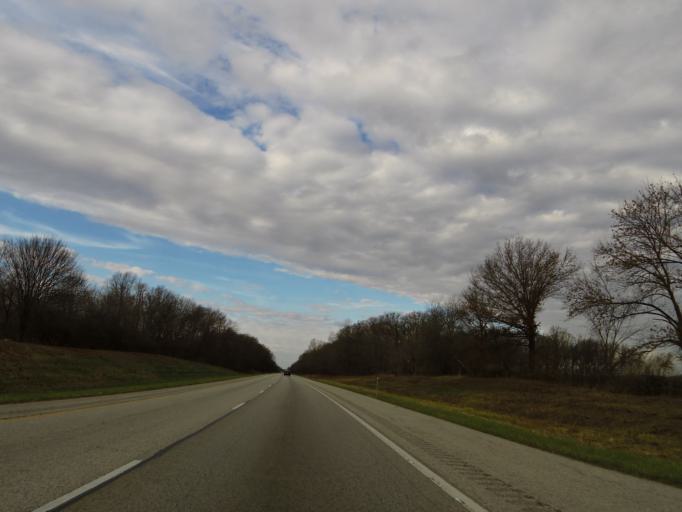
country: US
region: Illinois
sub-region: Washington County
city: Nashville
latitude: 38.4085
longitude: -89.4132
